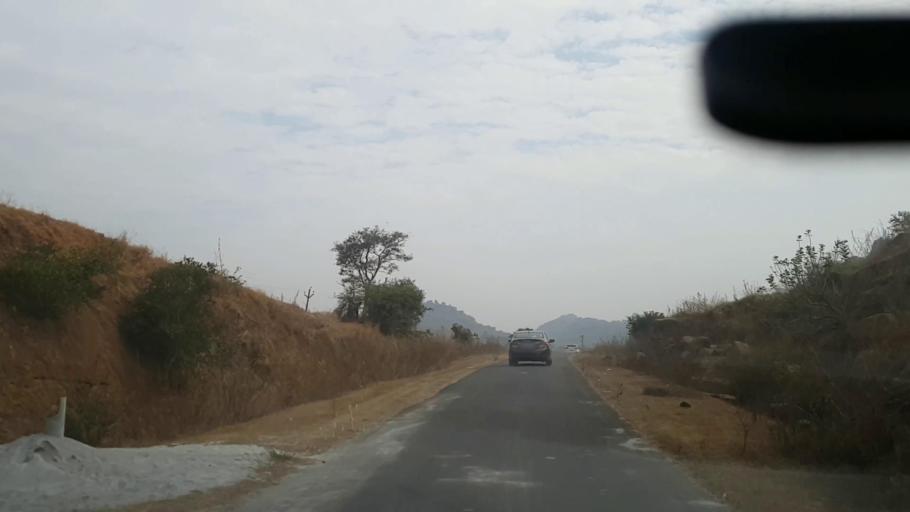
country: IN
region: Telangana
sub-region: Rangareddi
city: Lal Bahadur Nagar
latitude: 17.1785
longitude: 78.7785
